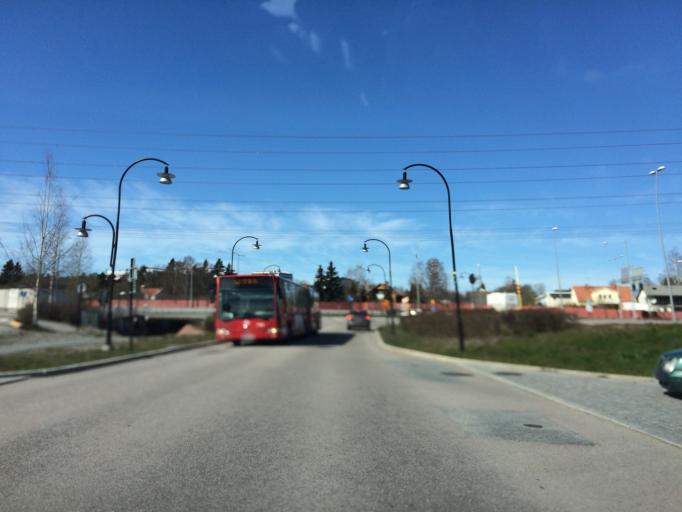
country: SE
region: Stockholm
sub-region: Sollentuna Kommun
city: Sollentuna
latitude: 59.4400
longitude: 17.9325
